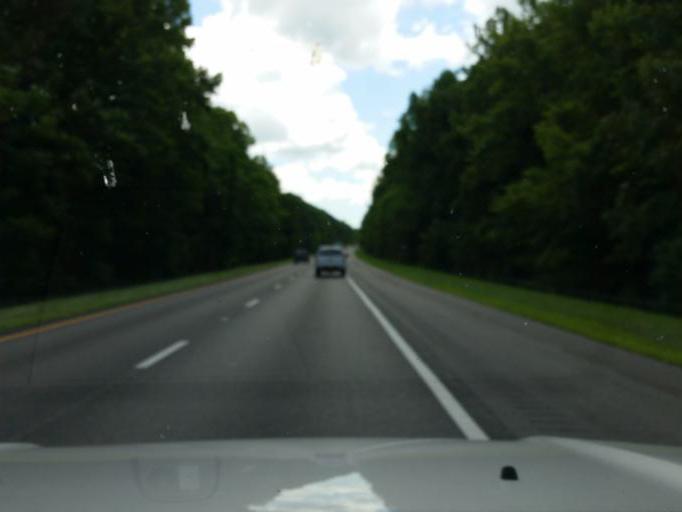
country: US
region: Virginia
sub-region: King William County
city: West Point
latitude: 37.4110
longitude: -76.7966
